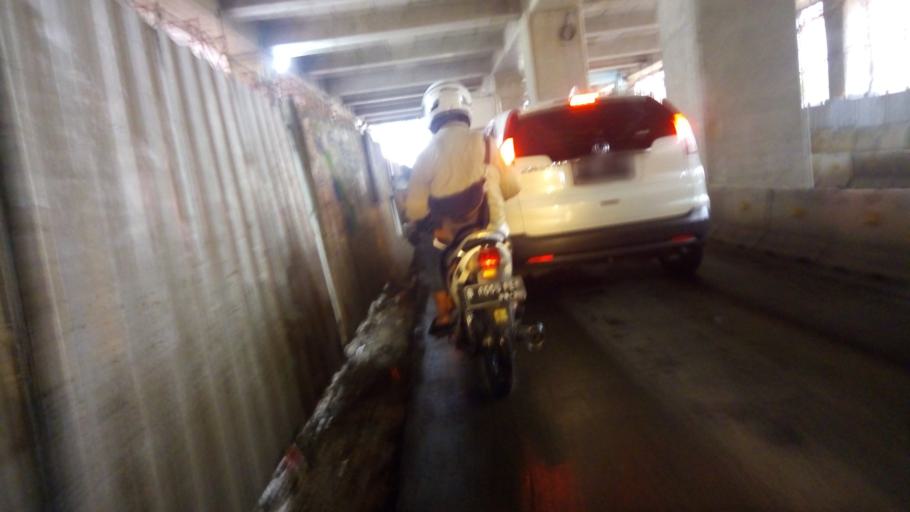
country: ID
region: Jakarta Raya
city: Jakarta
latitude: -6.2385
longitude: 106.7985
